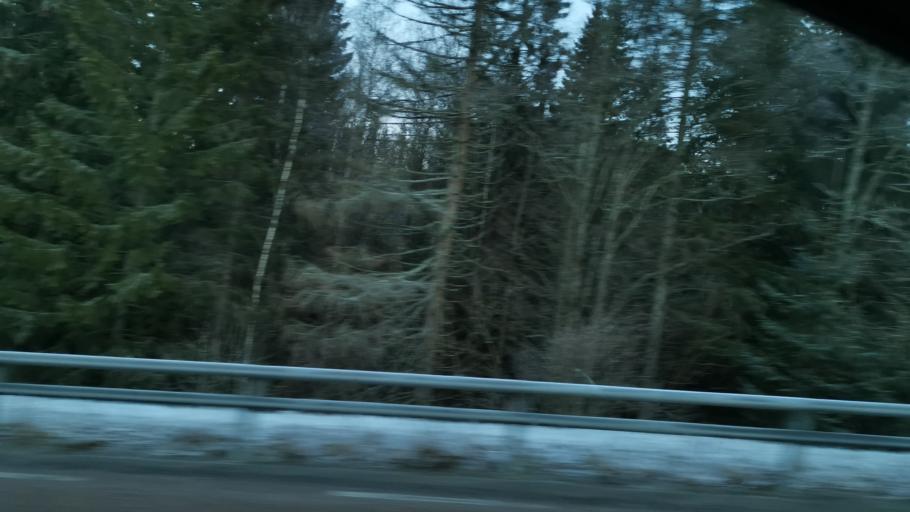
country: SE
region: Vaestra Goetaland
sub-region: Munkedals Kommun
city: Munkedal
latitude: 58.4118
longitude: 11.7336
